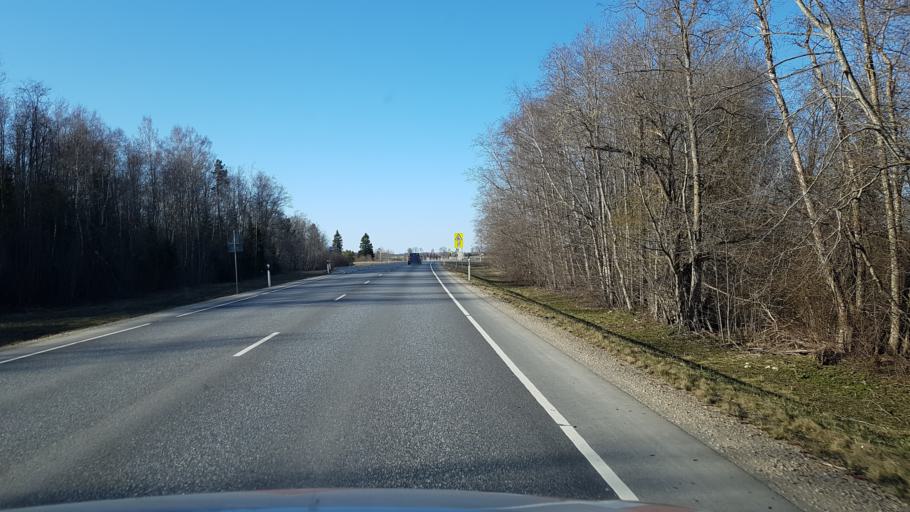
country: EE
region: Ida-Virumaa
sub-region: Johvi vald
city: Johvi
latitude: 59.3072
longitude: 27.3931
